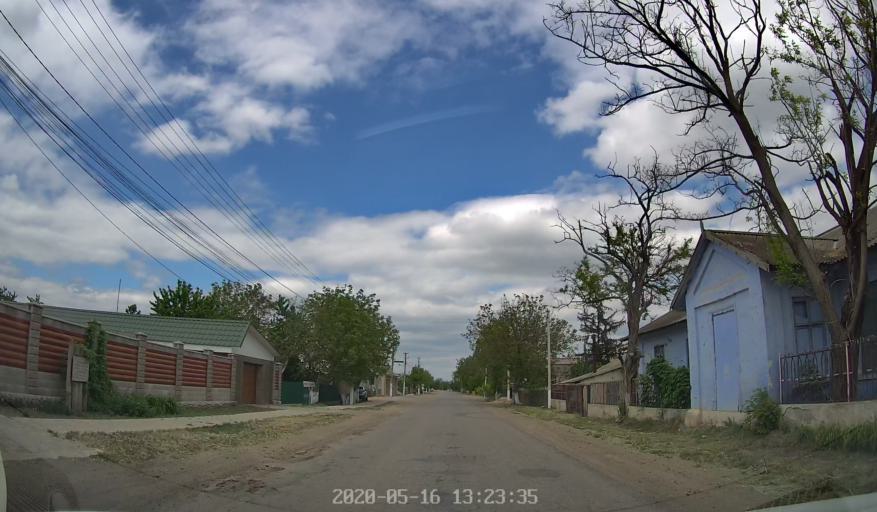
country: MD
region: Telenesti
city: Dnestrovsc
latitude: 46.5386
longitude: 30.0146
